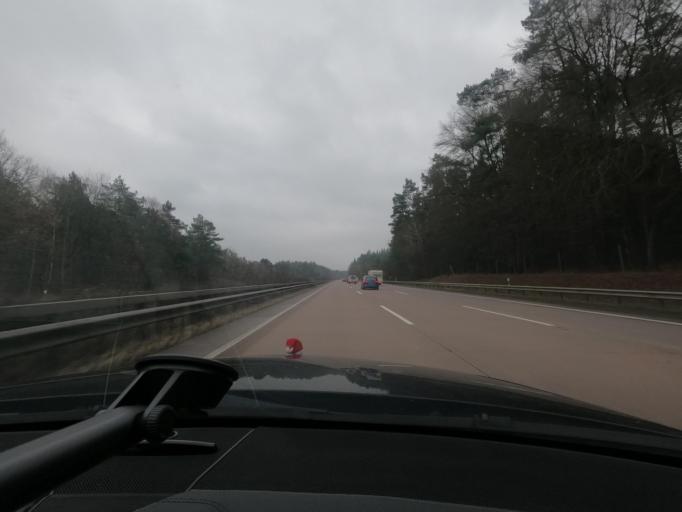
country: DE
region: Lower Saxony
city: Toppenstedt
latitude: 53.2674
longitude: 10.0856
